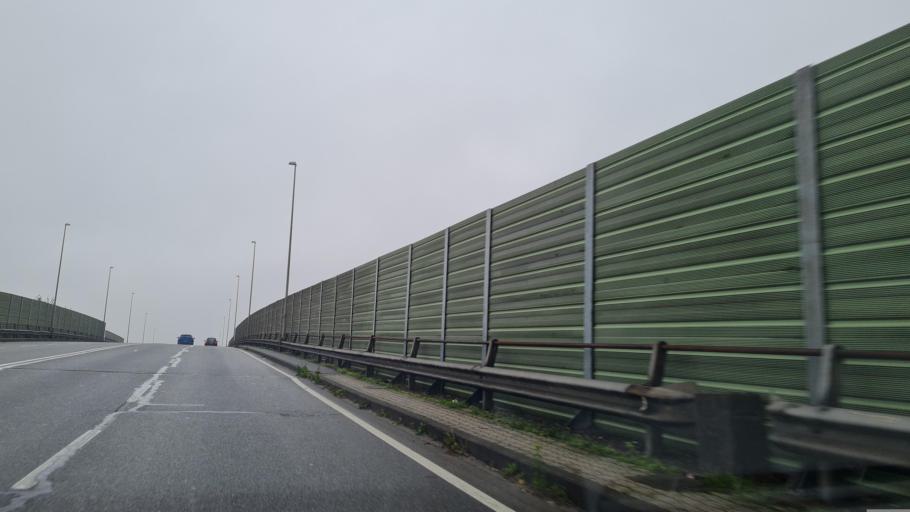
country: IT
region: Tuscany
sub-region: Provincia di Lucca
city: Lucca
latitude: 43.8399
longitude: 10.4761
